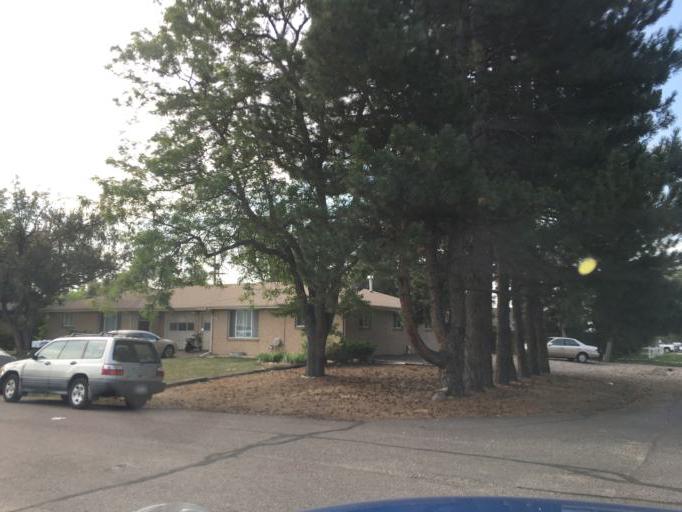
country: US
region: Colorado
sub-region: Jefferson County
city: Wheat Ridge
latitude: 39.7439
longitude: -105.1065
